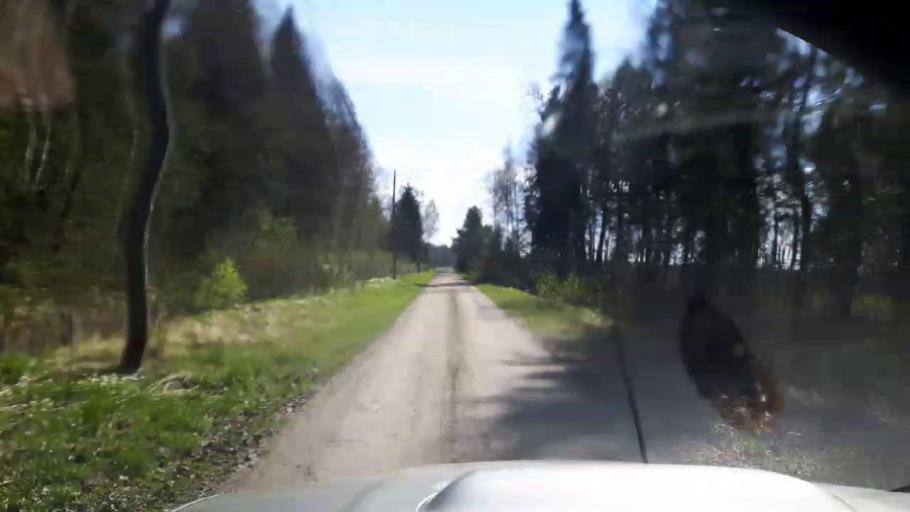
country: EE
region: Paernumaa
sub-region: Vaendra vald (alev)
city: Vandra
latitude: 58.5045
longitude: 24.9735
